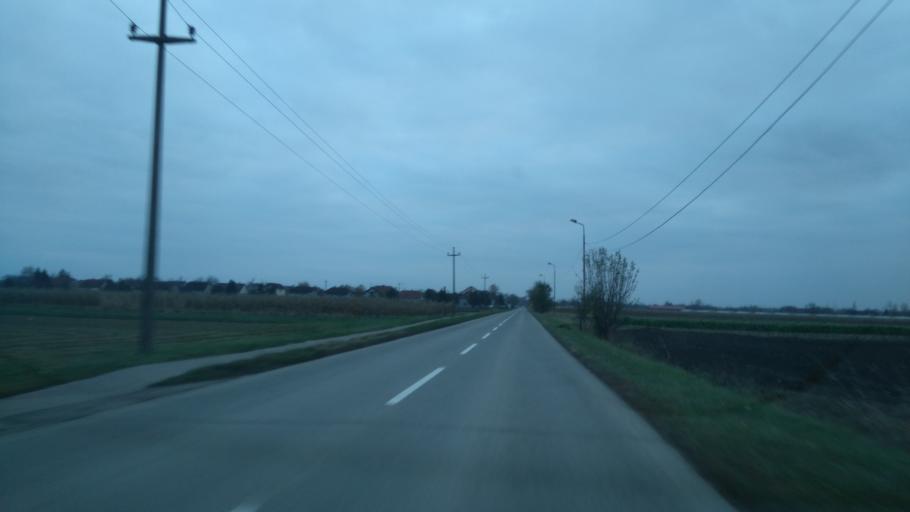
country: RS
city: Mol
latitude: 45.7782
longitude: 20.1281
